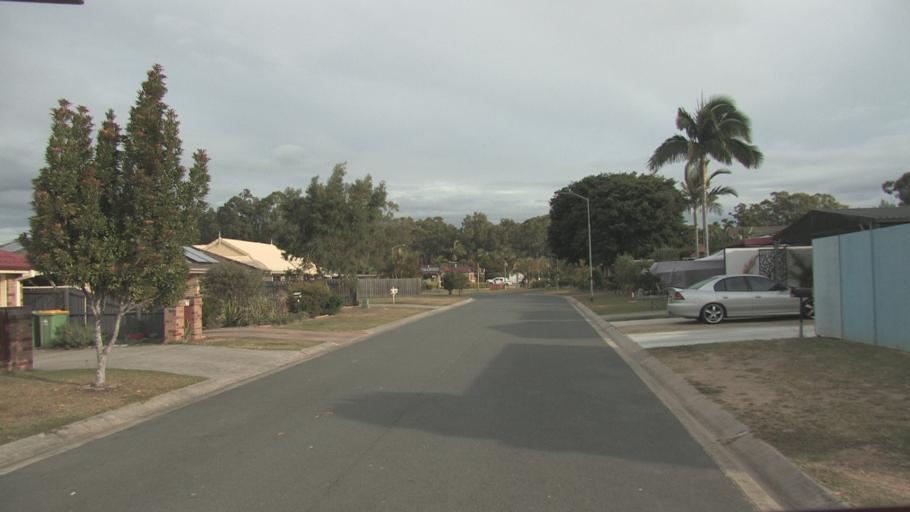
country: AU
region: Queensland
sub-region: Logan
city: Park Ridge South
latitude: -27.6767
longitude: 153.0183
